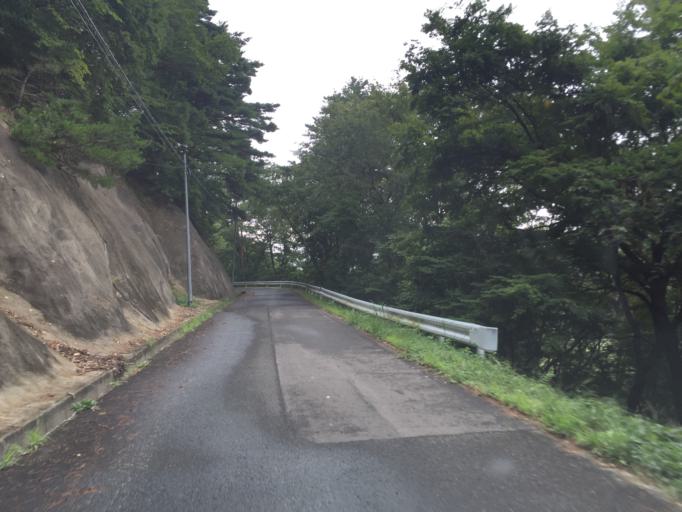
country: JP
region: Fukushima
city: Fukushima-shi
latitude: 37.7986
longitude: 140.3722
